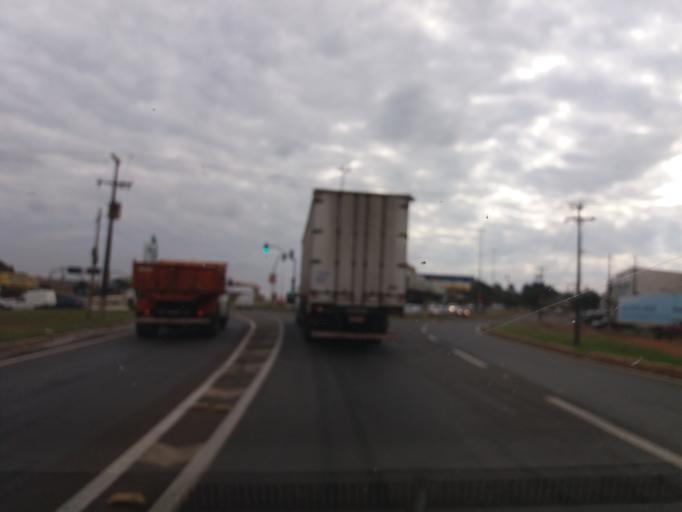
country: BR
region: Parana
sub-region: Cascavel
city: Cascavel
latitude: -24.9642
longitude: -53.4066
